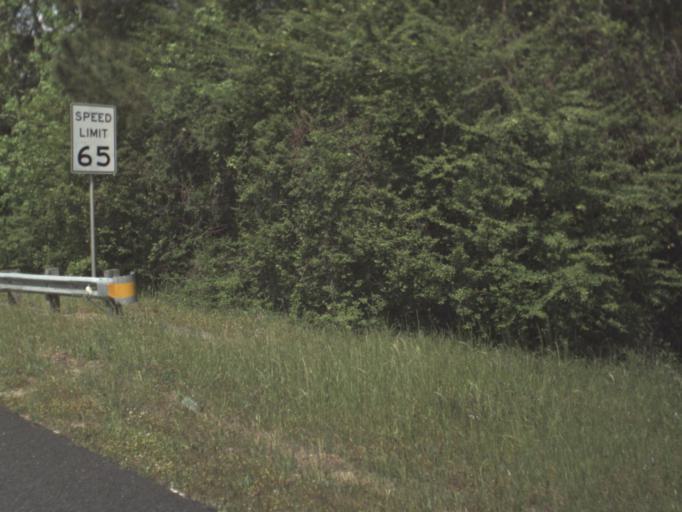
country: US
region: Florida
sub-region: Escambia County
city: Century
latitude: 30.9167
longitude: -87.3149
